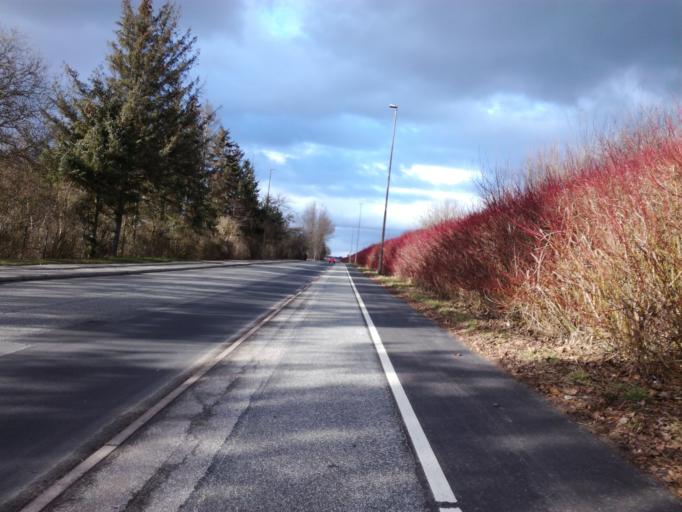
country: DK
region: South Denmark
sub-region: Fredericia Kommune
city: Fredericia
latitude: 55.5912
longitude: 9.7676
